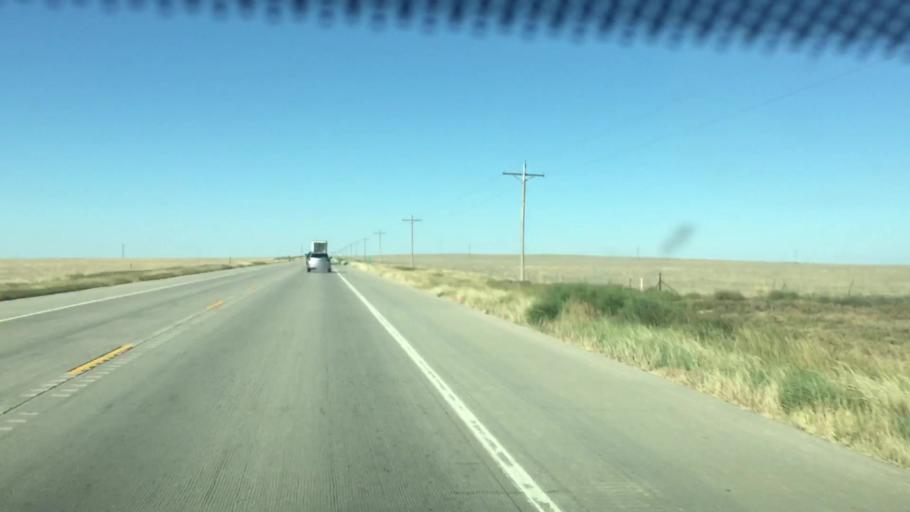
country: US
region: Colorado
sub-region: Prowers County
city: Lamar
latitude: 38.2521
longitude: -102.7240
